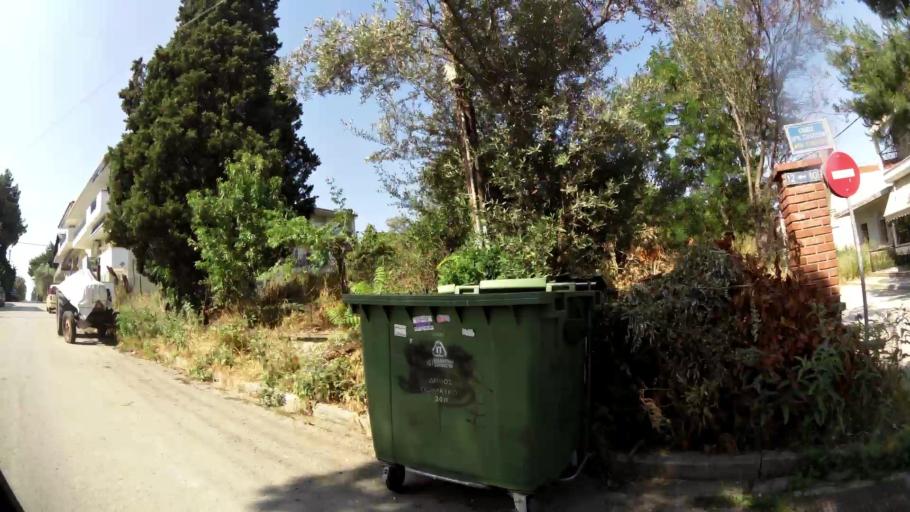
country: GR
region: Central Macedonia
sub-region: Nomos Thessalonikis
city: Peraia
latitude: 40.5004
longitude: 22.9283
